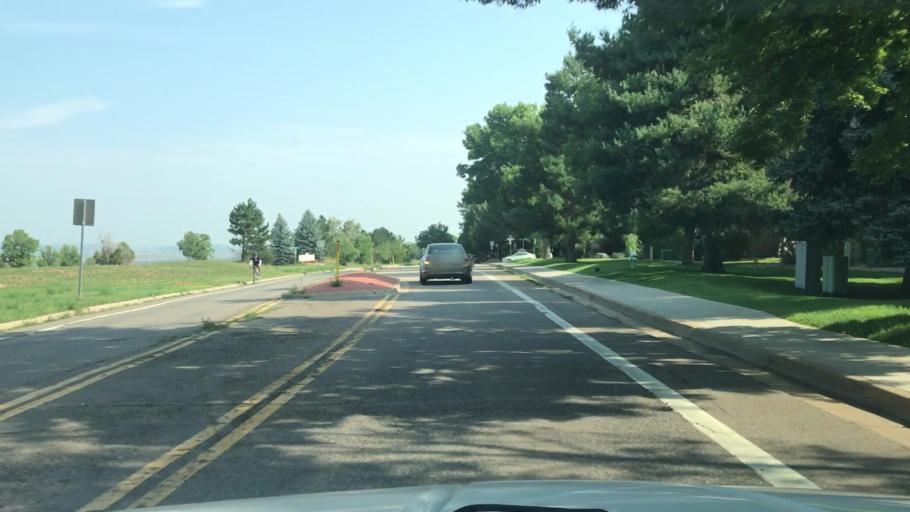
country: US
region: Colorado
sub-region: Boulder County
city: Gunbarrel
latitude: 40.0582
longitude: -105.2160
